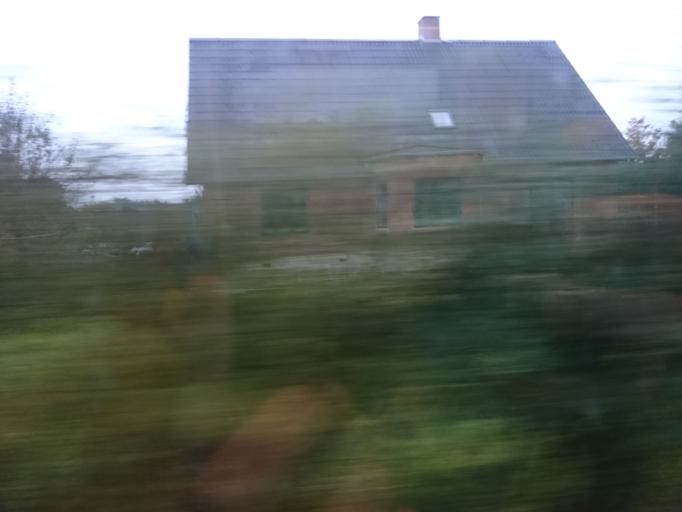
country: DK
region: Central Jutland
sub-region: Arhus Kommune
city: Marslet
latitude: 56.0697
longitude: 10.1614
